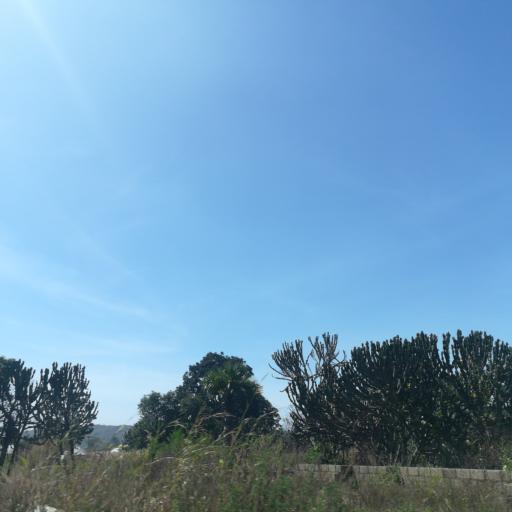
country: NG
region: Plateau
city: Bukuru
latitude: 9.7586
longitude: 8.8670
